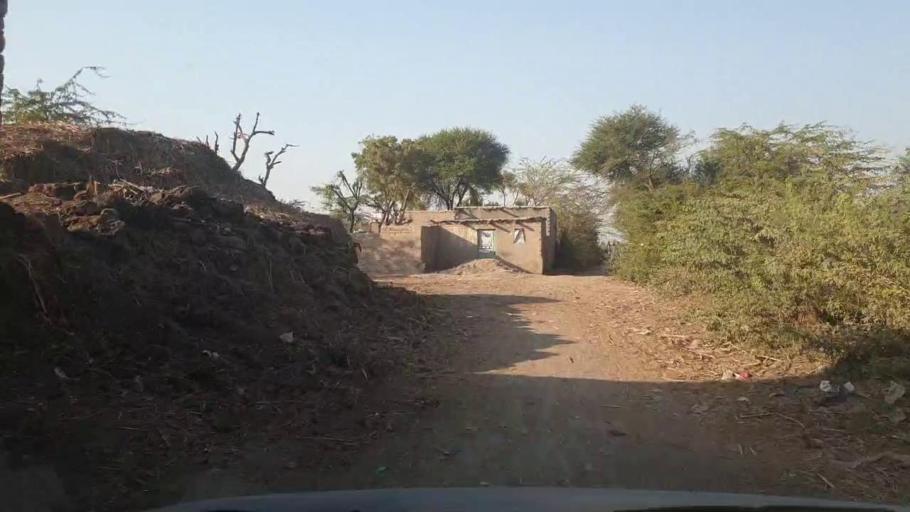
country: PK
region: Sindh
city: Chambar
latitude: 25.3076
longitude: 68.8741
